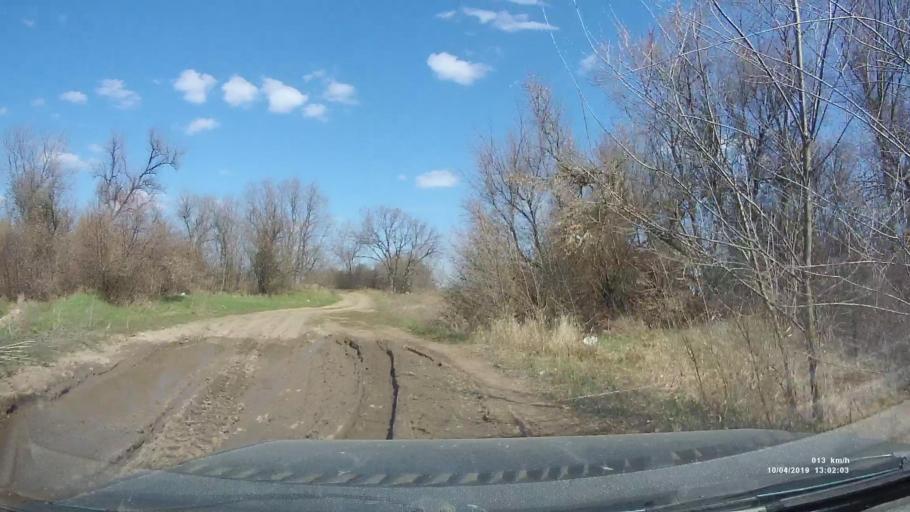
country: RU
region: Rostov
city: Masalovka
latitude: 48.3805
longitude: 40.2301
